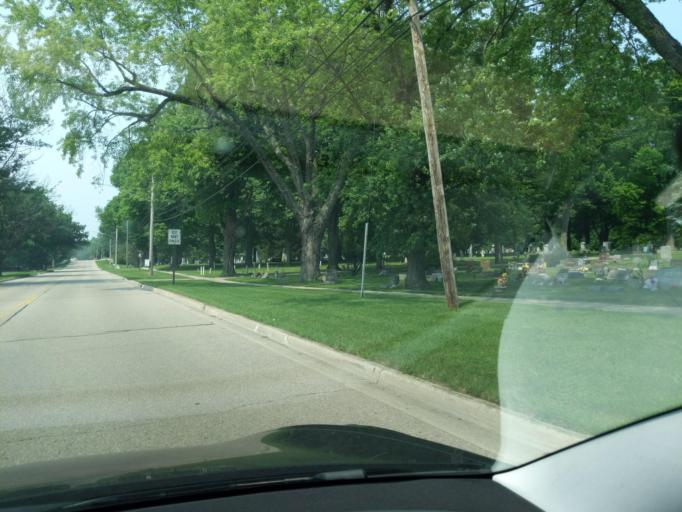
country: US
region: Michigan
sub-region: Clinton County
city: DeWitt
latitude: 42.8471
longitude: -84.5690
